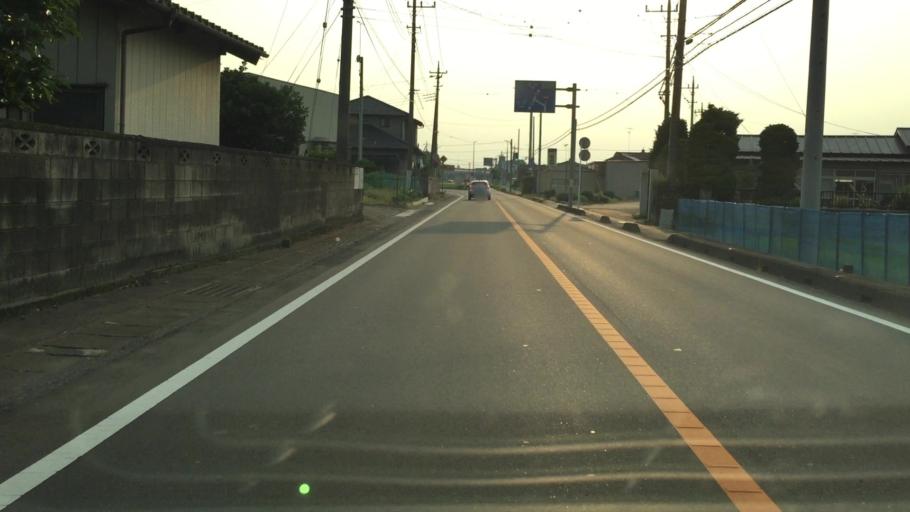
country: JP
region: Gunma
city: Tatebayashi
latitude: 36.2272
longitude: 139.5793
